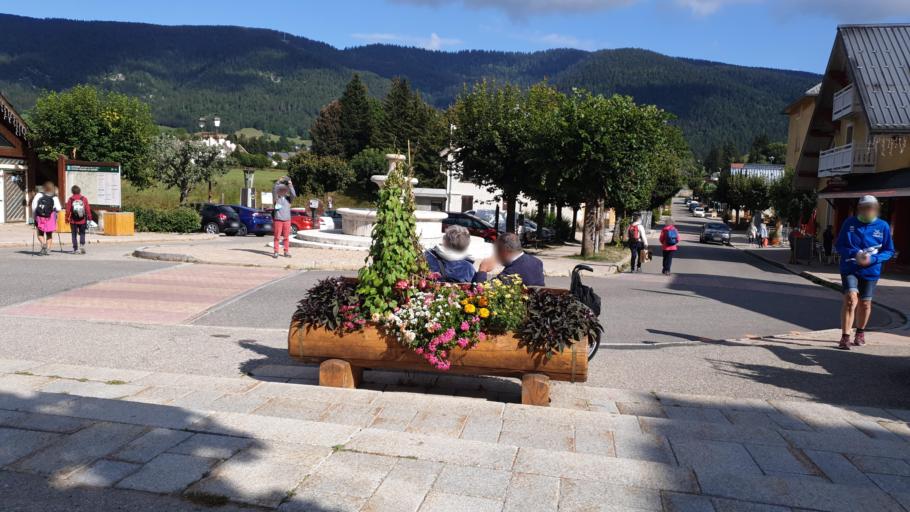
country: FR
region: Rhone-Alpes
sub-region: Departement de l'Isere
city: Autrans
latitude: 45.1749
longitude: 5.5423
